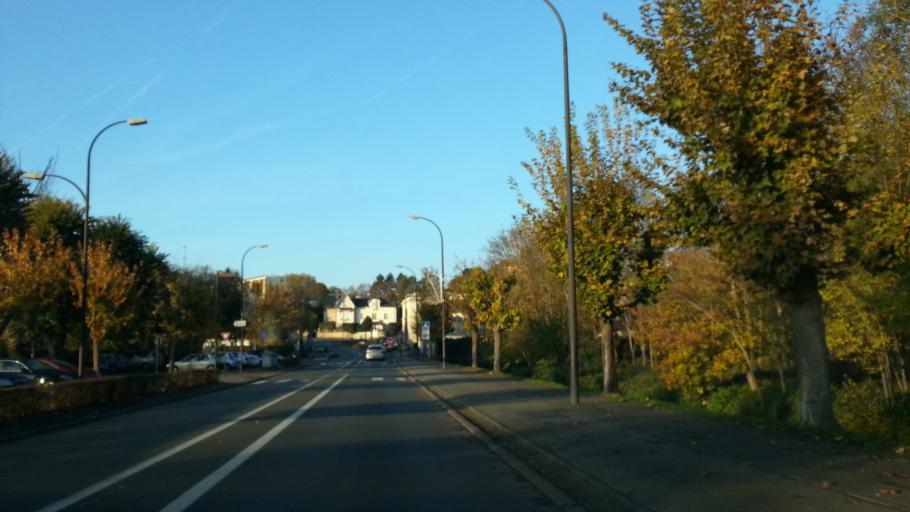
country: FR
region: Picardie
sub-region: Departement de l'Oise
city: Chantilly
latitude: 49.1966
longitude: 2.4640
